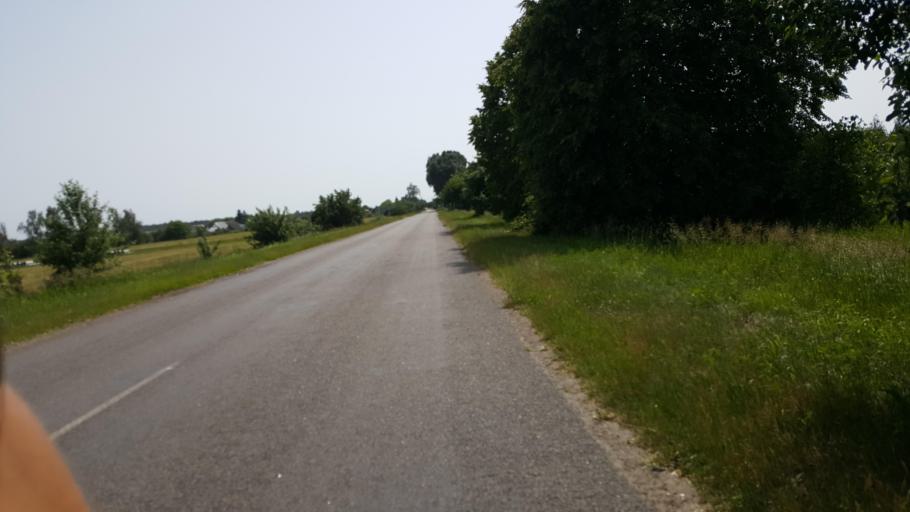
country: BY
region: Brest
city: Kamyanyets
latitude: 52.4114
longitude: 23.7993
